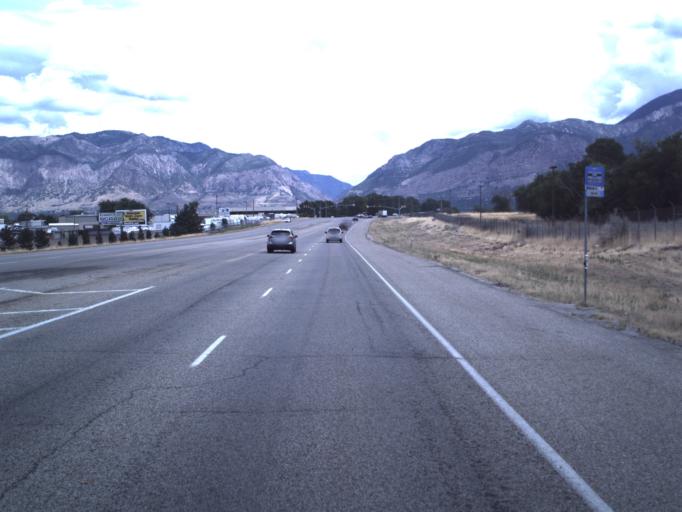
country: US
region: Utah
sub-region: Weber County
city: Riverdale
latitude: 41.2030
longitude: -112.0119
